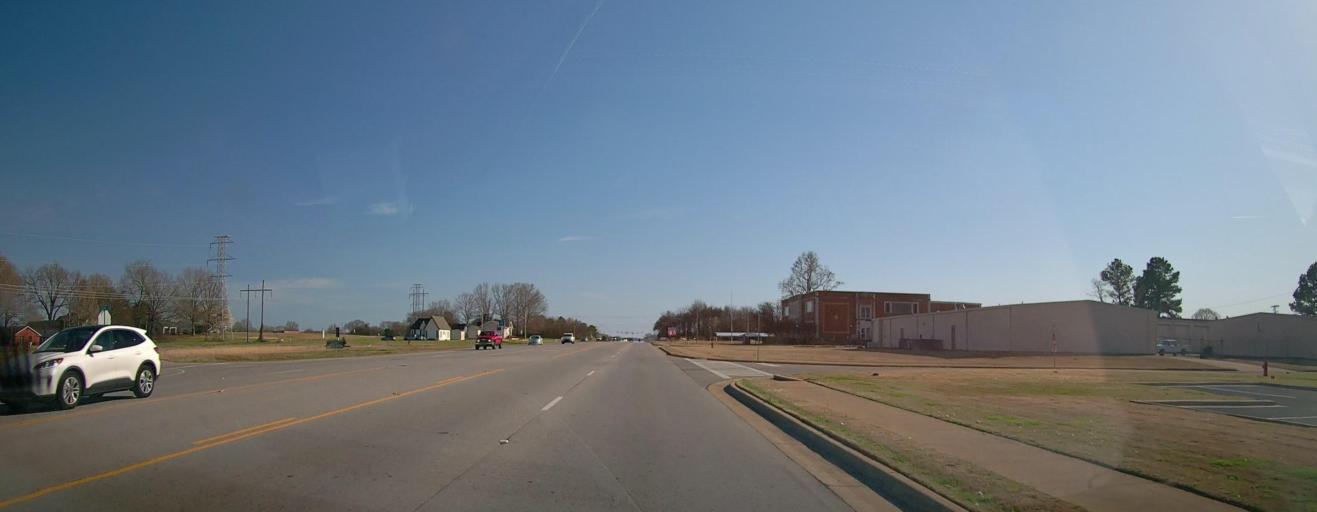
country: US
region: Alabama
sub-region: Colbert County
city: Muscle Shoals
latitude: 34.7351
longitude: -87.6353
